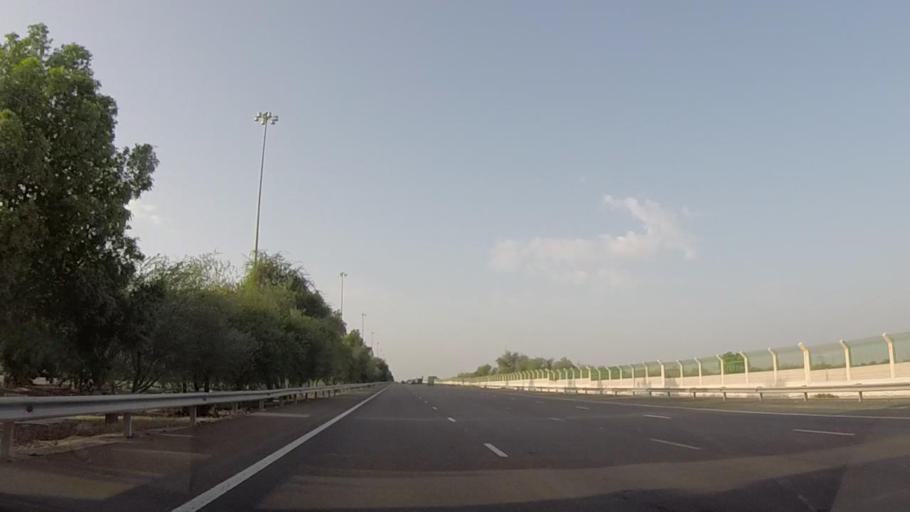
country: AE
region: Dubai
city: Dubai
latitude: 24.7601
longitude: 54.8419
